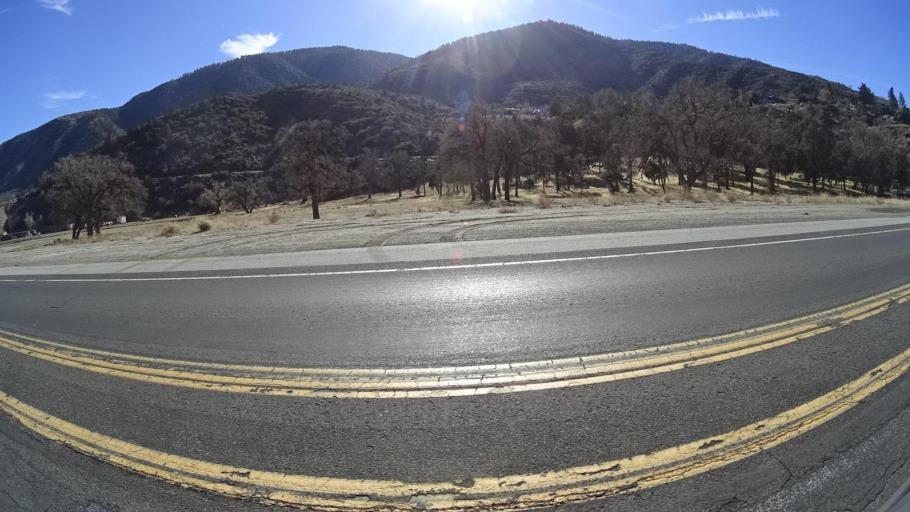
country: US
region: California
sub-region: Kern County
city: Frazier Park
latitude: 34.8191
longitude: -118.9401
